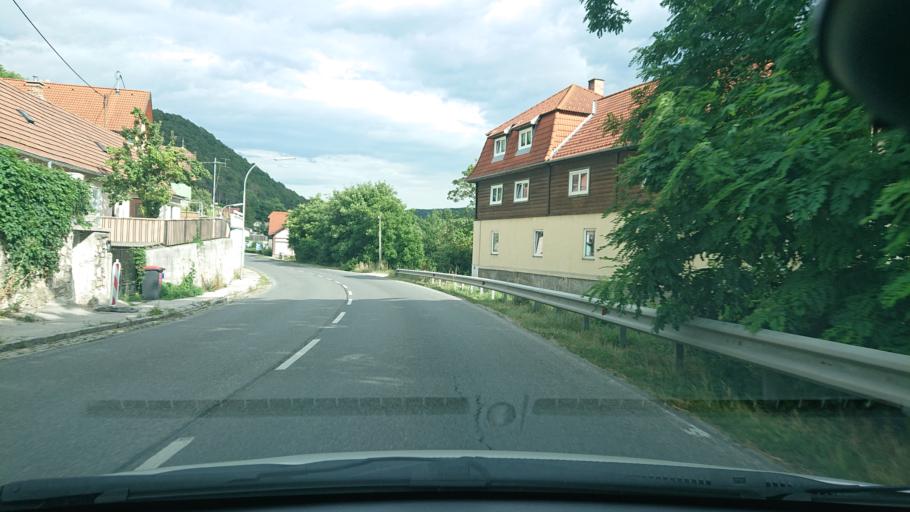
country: AT
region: Lower Austria
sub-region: Politischer Bezirk Baden
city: Berndorf
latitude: 47.9428
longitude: 16.1329
